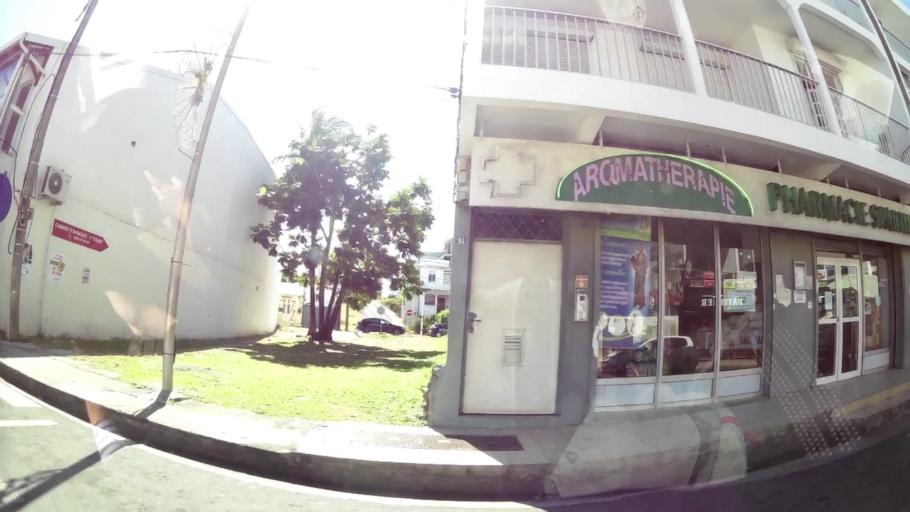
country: GP
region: Guadeloupe
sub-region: Guadeloupe
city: Le Moule
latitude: 16.3297
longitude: -61.3441
